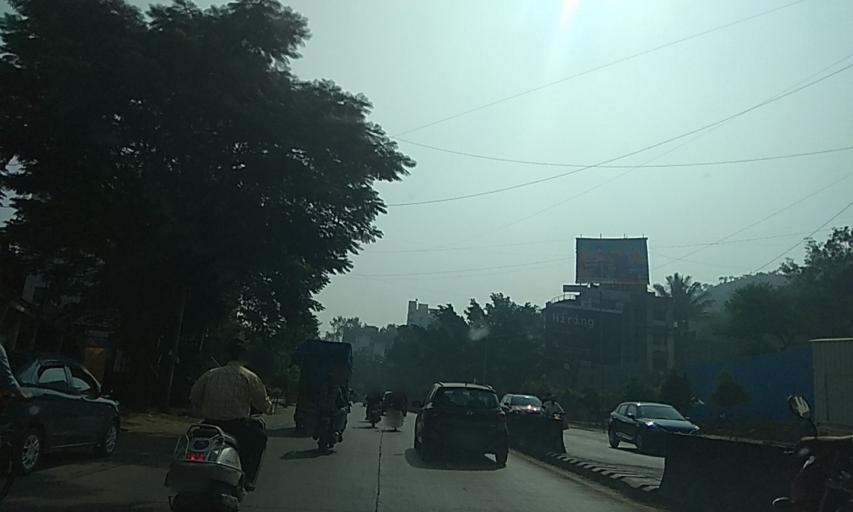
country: IN
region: Maharashtra
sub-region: Pune Division
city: Khadki
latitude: 18.5600
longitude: 73.7890
